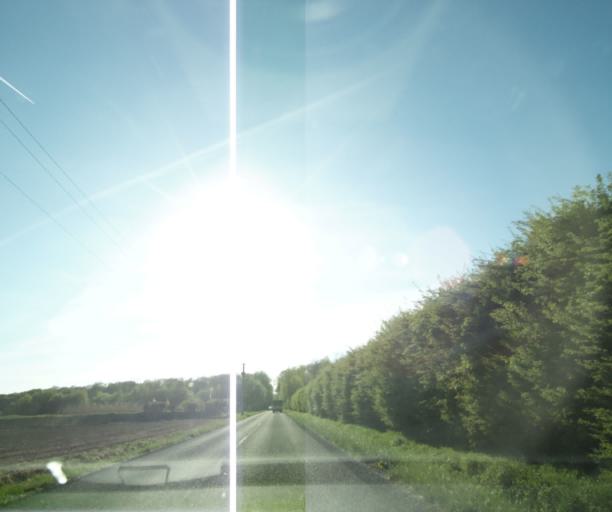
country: FR
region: Ile-de-France
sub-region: Departement de Seine-et-Marne
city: La Chapelle-Gauthier
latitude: 48.5135
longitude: 2.9413
